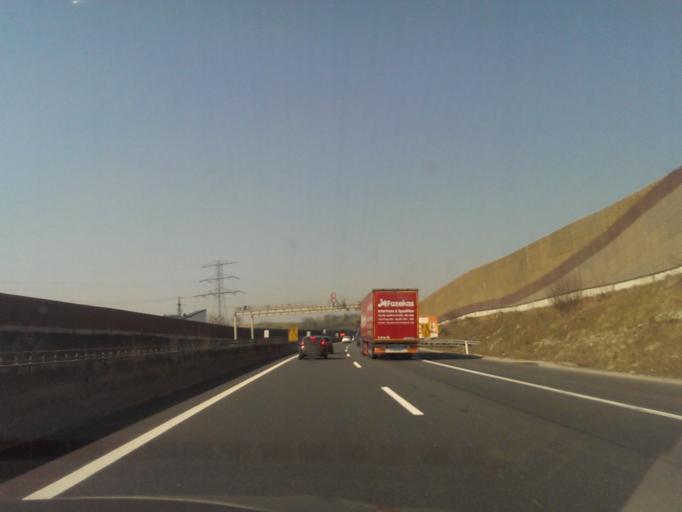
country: AT
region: Upper Austria
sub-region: Politischer Bezirk Vocklabruck
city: Wolfsegg am Hausruck
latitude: 48.1771
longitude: 13.7006
